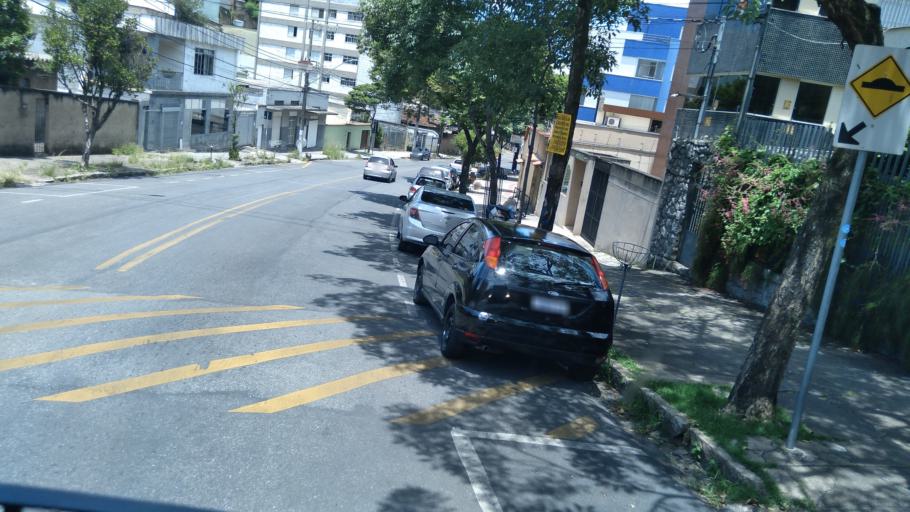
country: BR
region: Minas Gerais
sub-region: Belo Horizonte
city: Belo Horizonte
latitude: -19.9160
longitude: -43.9913
